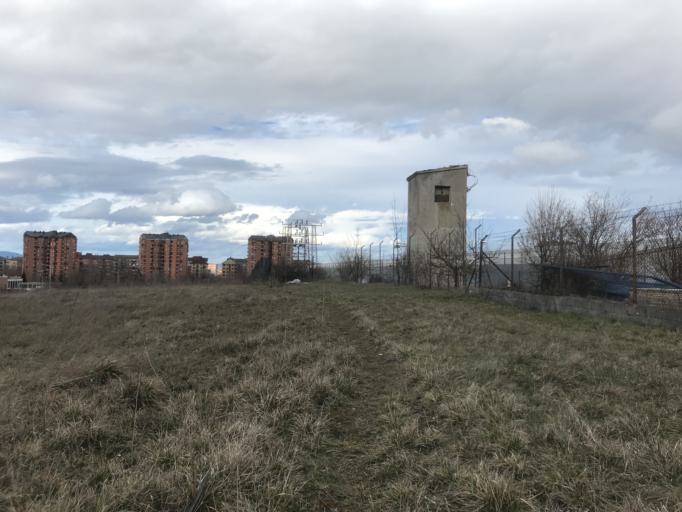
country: ES
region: Basque Country
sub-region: Provincia de Alava
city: Gasteiz / Vitoria
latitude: 42.8311
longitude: -2.6683
